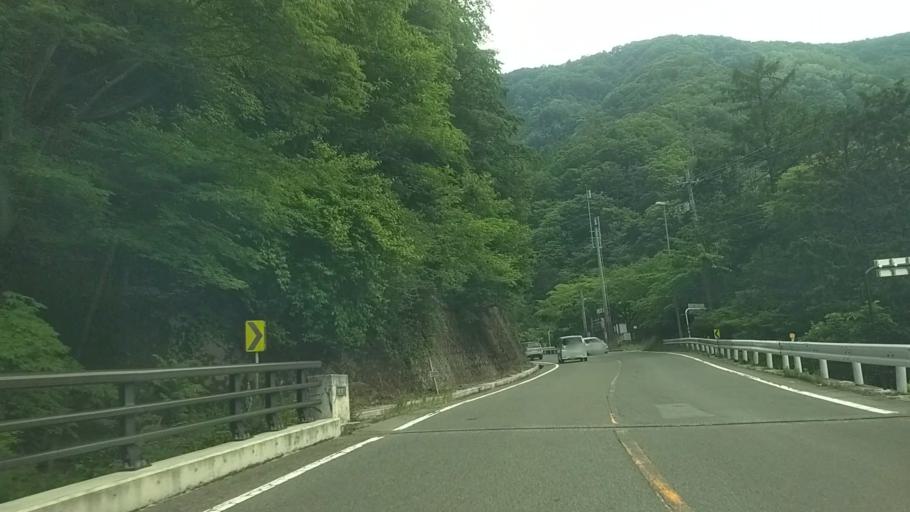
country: JP
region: Yamanashi
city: Isawa
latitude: 35.5589
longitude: 138.5901
